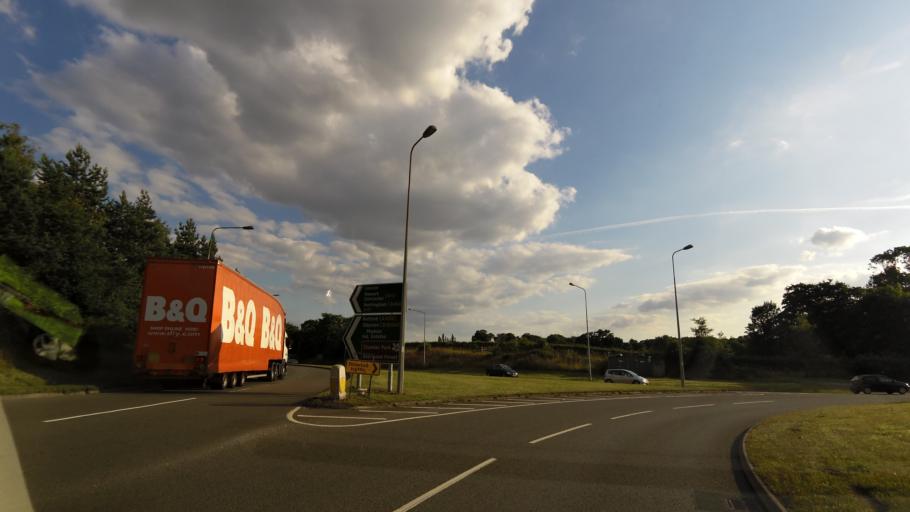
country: GB
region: England
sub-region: Nottinghamshire
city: Worksop
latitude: 53.3024
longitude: -1.1362
